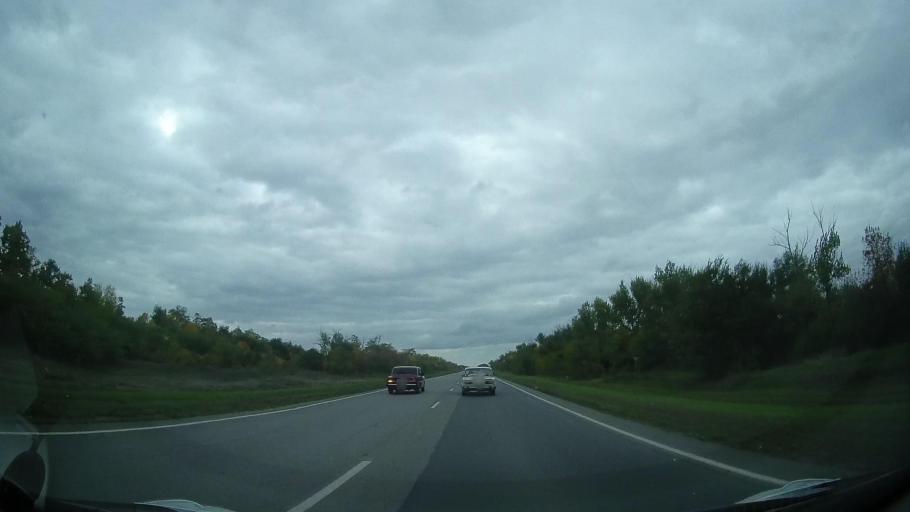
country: RU
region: Rostov
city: Yegorlykskaya
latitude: 46.5468
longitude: 40.7550
